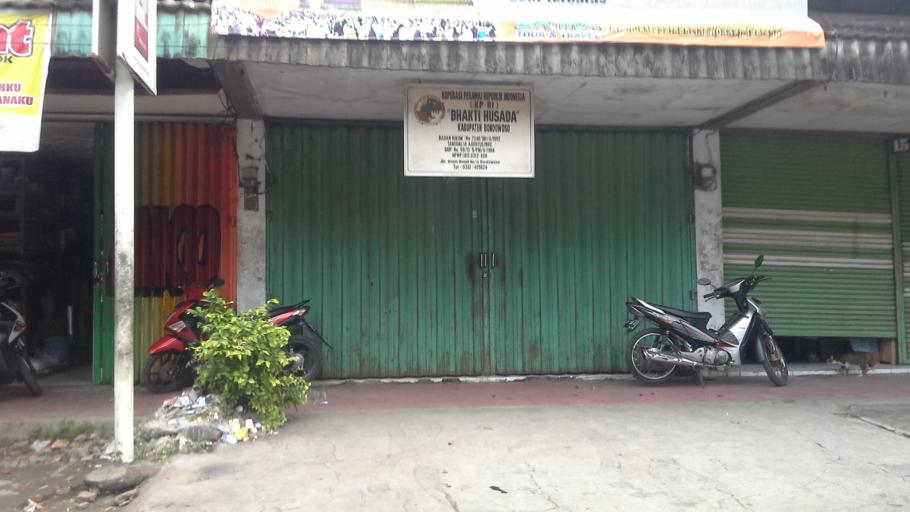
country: ID
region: East Java
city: Bondowoso
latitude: -7.9156
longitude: 113.8303
